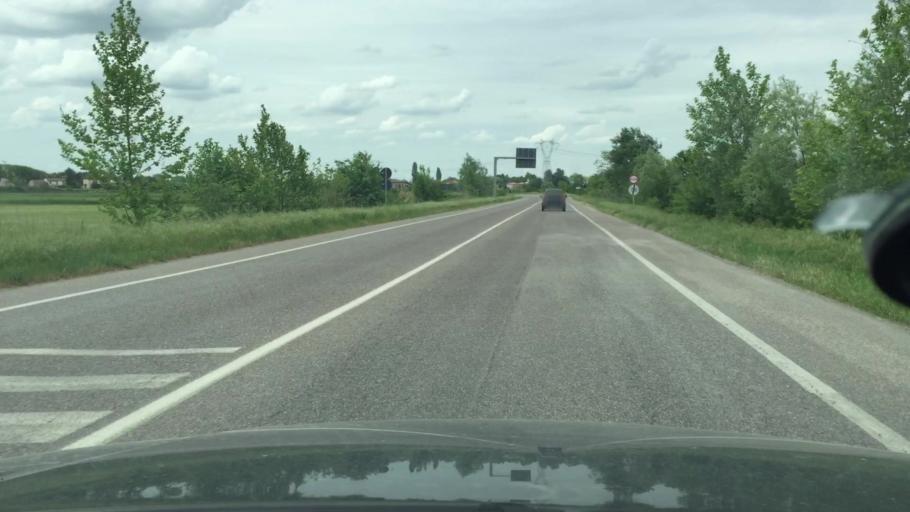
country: IT
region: Emilia-Romagna
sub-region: Provincia di Ferrara
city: Cona
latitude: 44.8065
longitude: 11.7193
